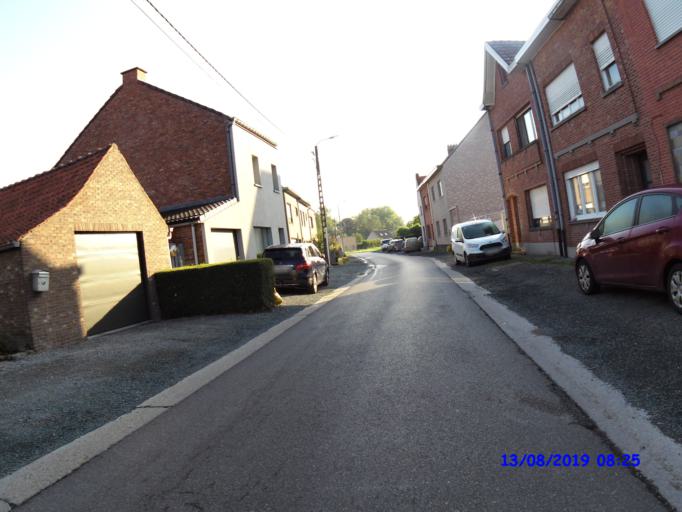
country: BE
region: Flanders
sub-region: Provincie Oost-Vlaanderen
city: Lebbeke
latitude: 51.0158
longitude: 4.1259
